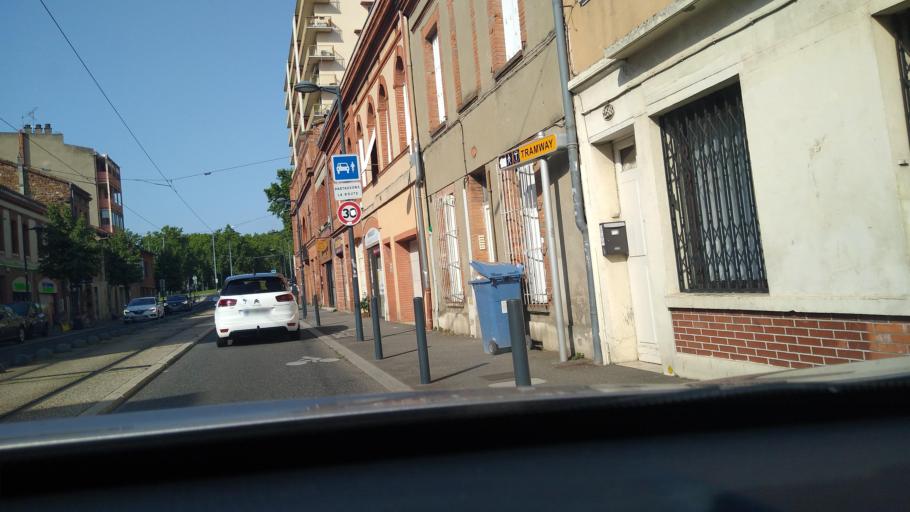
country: FR
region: Midi-Pyrenees
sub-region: Departement de la Haute-Garonne
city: Toulouse
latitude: 43.5915
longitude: 1.4335
